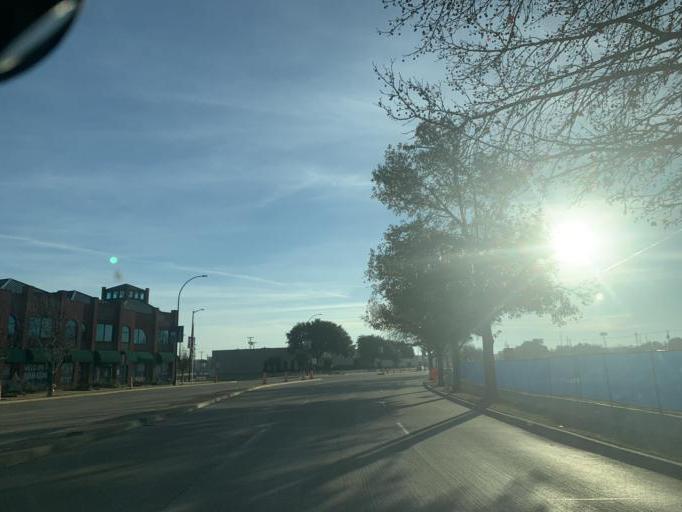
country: US
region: Texas
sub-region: Tarrant County
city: Arlington
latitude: 32.7499
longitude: -97.0806
